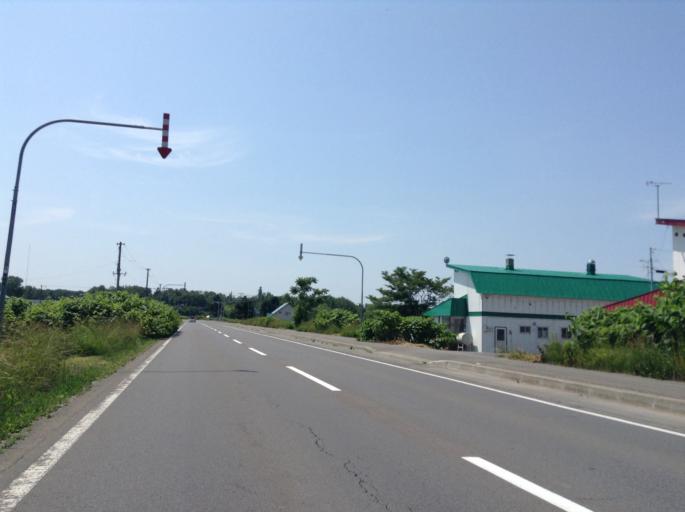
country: JP
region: Hokkaido
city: Nayoro
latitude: 44.3537
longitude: 142.4733
